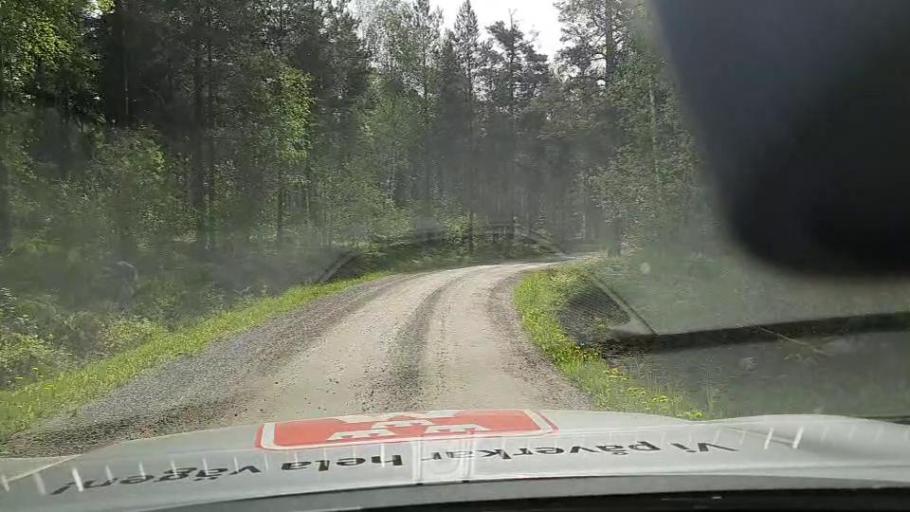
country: SE
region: Soedermanland
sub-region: Flens Kommun
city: Malmkoping
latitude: 59.2614
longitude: 16.8700
